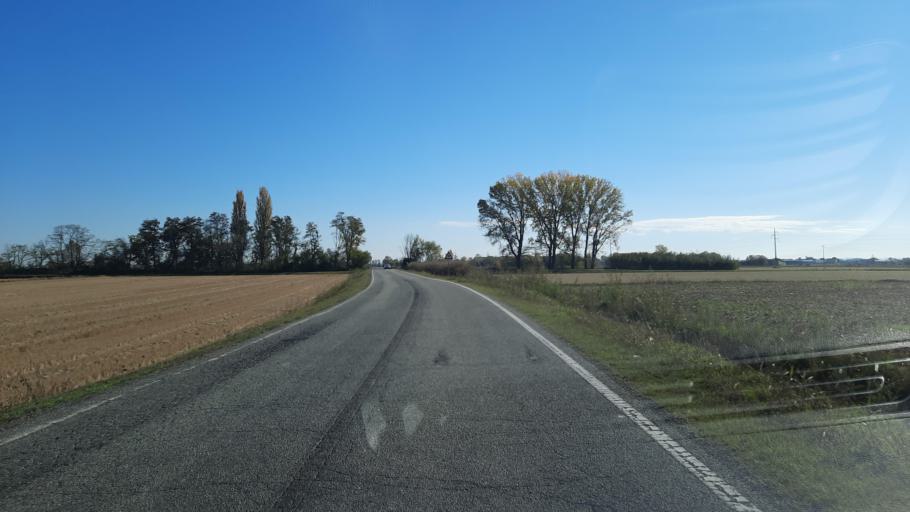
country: IT
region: Piedmont
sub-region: Provincia di Alessandria
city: Villanova Monferrato
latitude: 45.1827
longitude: 8.4463
